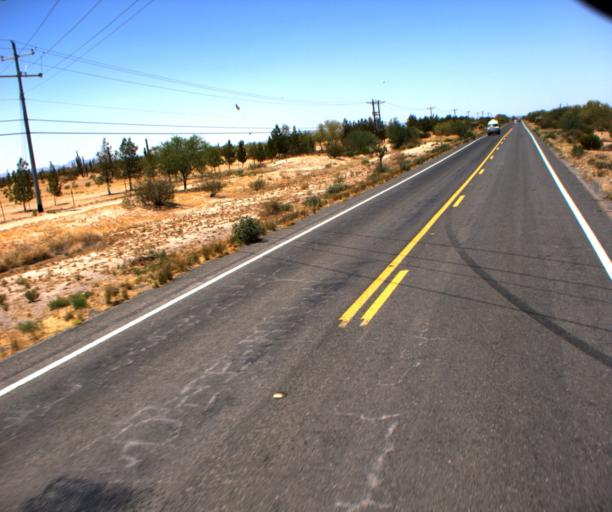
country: US
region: Arizona
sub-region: Pinal County
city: Florence
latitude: 32.9439
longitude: -111.3196
